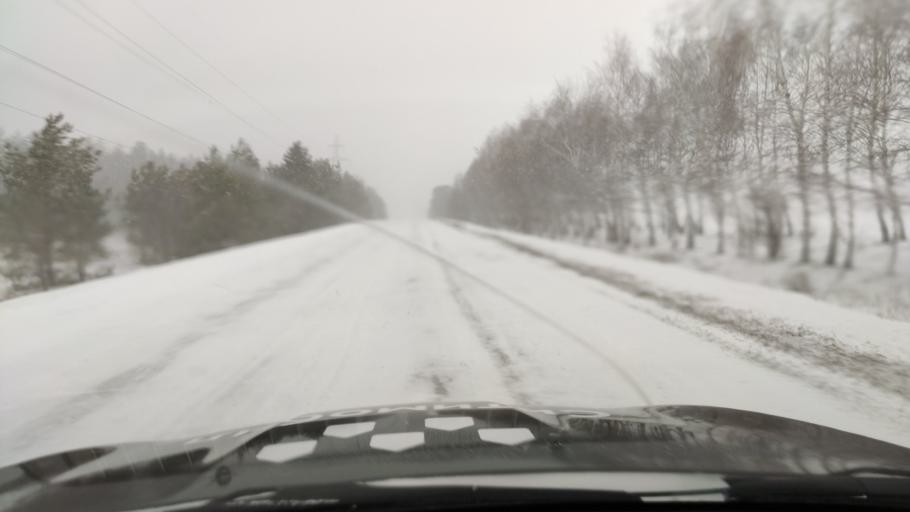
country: RU
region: Samara
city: Povolzhskiy
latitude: 53.5243
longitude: 49.7049
